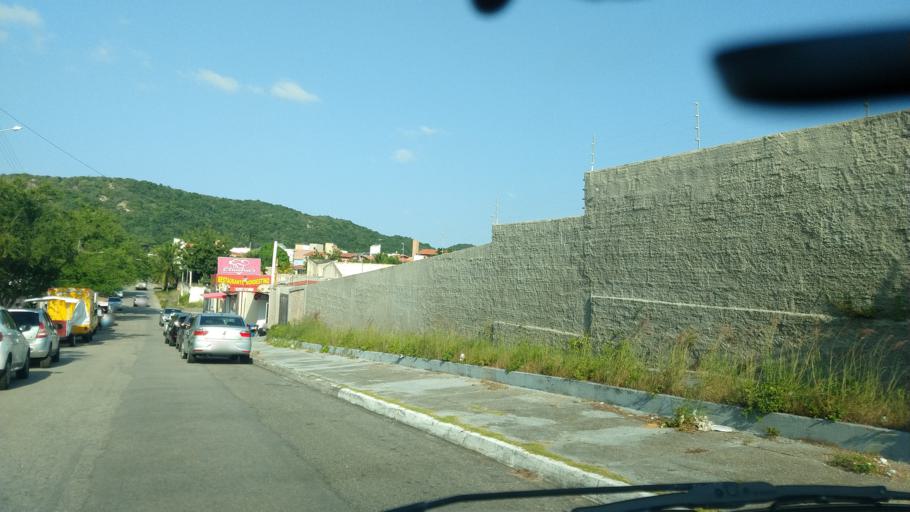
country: BR
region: Rio Grande do Norte
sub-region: Natal
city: Natal
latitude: -5.8439
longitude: -35.2003
